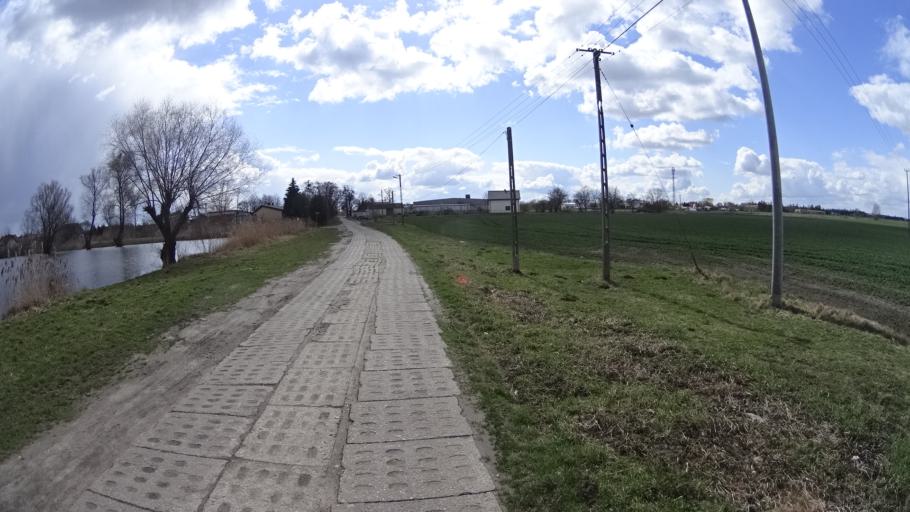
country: PL
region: Masovian Voivodeship
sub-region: Powiat warszawski zachodni
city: Jozefow
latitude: 52.2180
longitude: 20.7151
